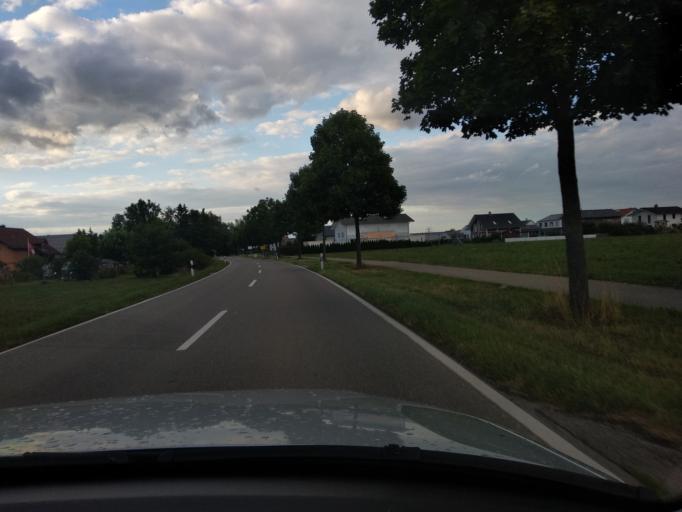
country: DE
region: Bavaria
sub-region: Swabia
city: Woringen
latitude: 47.9163
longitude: 10.2030
